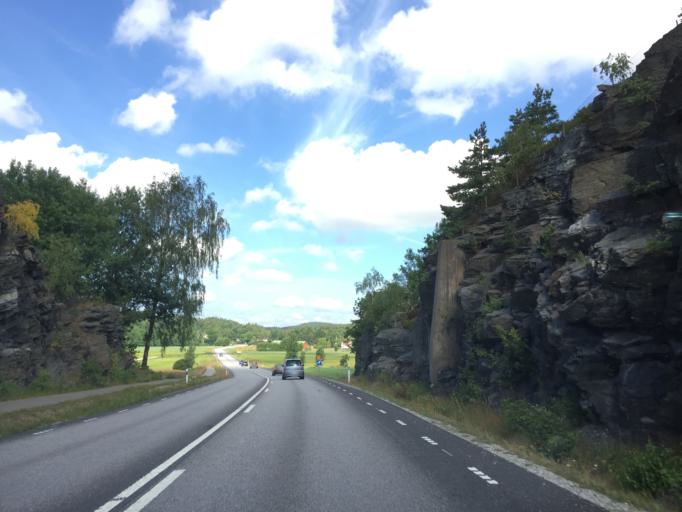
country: SE
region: Vaestra Goetaland
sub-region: Orust
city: Henan
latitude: 58.3104
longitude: 11.6964
